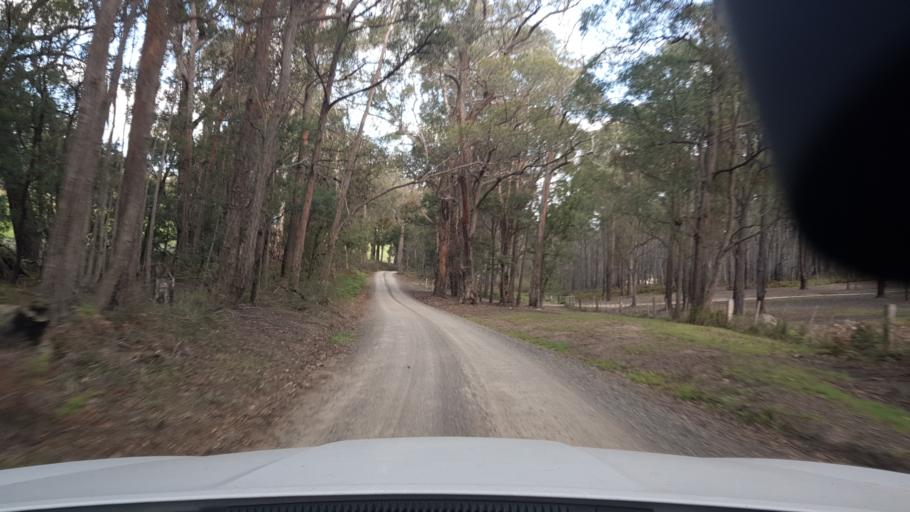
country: AU
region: Victoria
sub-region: East Gippsland
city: Bairnsdale
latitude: -37.7663
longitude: 147.5684
